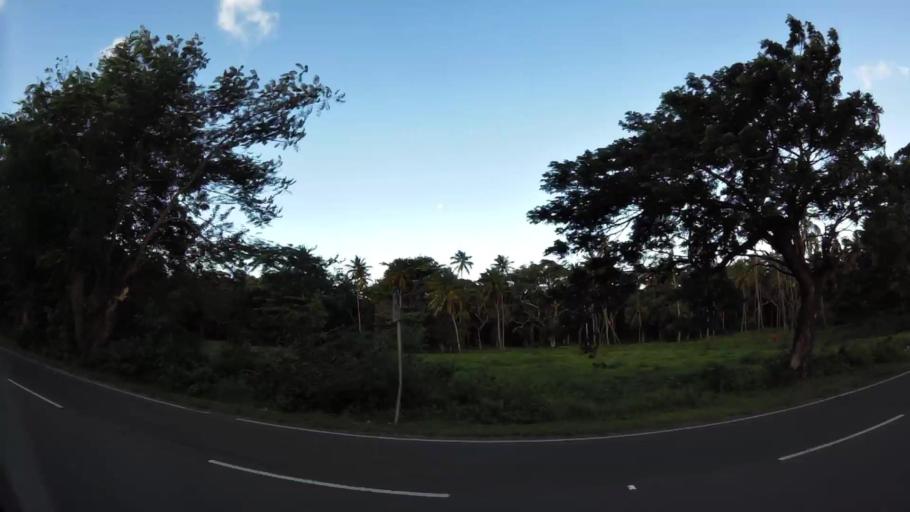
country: LC
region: Castries Quarter
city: Bisee
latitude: 14.0357
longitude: -60.9692
